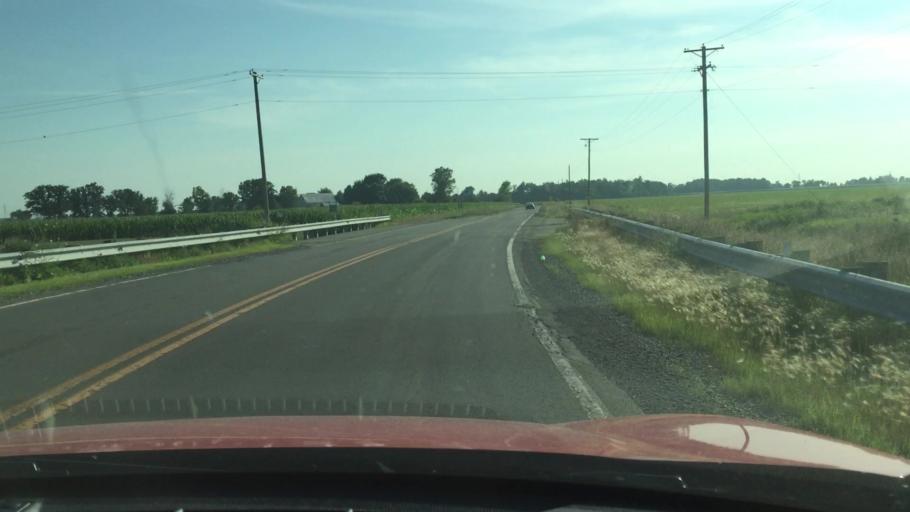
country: US
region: Ohio
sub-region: Hardin County
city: Ada
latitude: 40.7018
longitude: -83.8485
